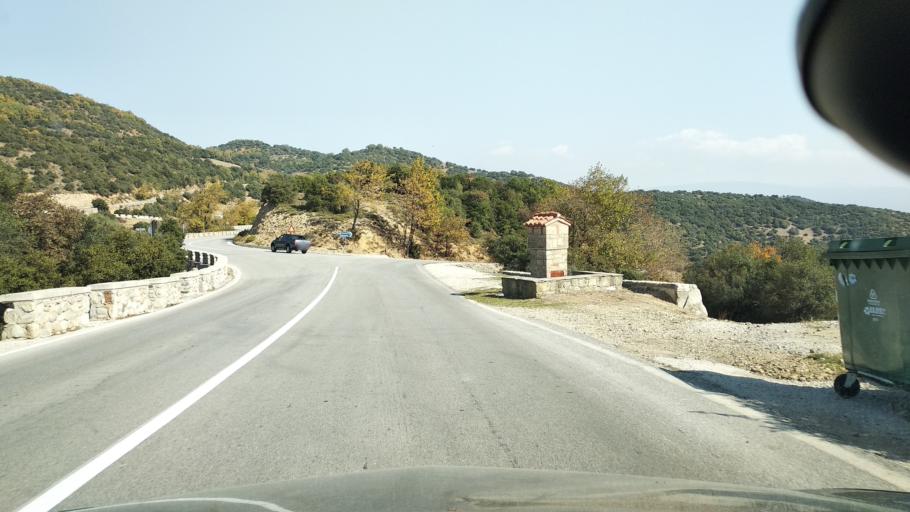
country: GR
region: Thessaly
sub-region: Trikala
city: Kalampaka
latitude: 39.7161
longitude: 21.6408
